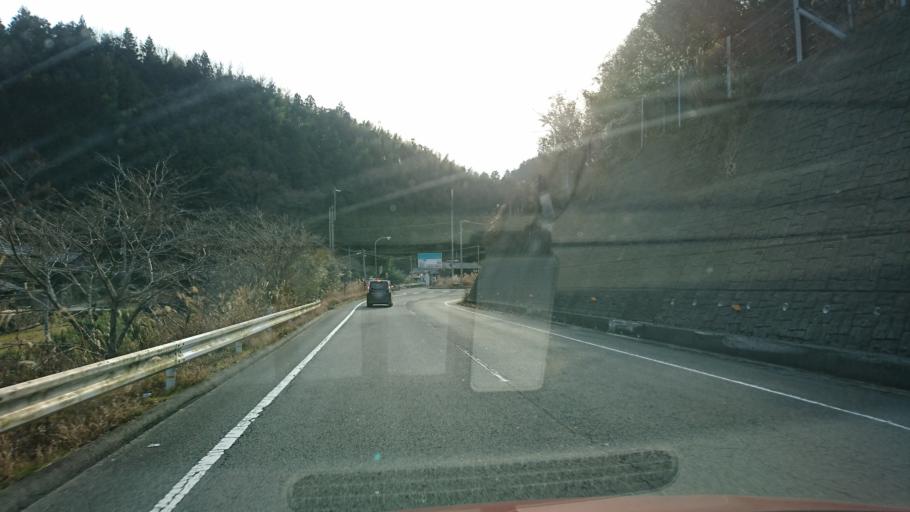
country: JP
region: Ehime
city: Hojo
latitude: 33.9178
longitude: 132.8853
